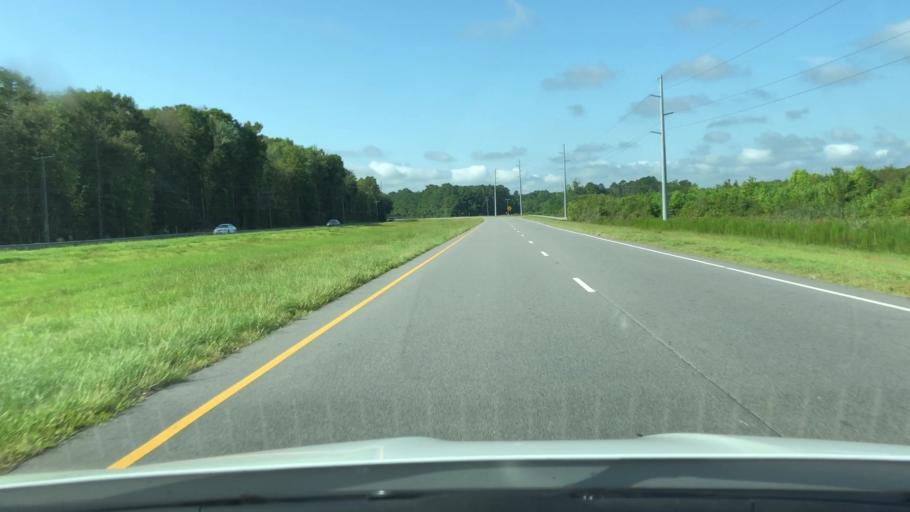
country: US
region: North Carolina
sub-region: Pasquotank County
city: Elizabeth City
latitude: 36.4314
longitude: -76.3403
